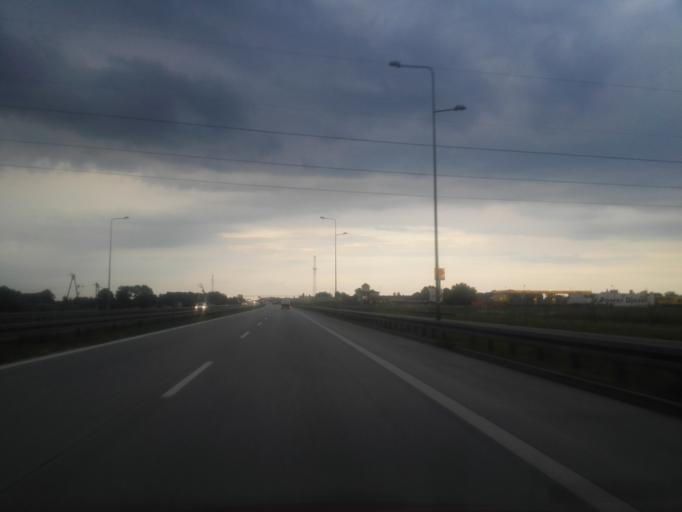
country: PL
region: Lodz Voivodeship
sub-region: Piotrkow Trybunalski
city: Piotrkow Trybunalski
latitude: 51.4421
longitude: 19.6773
